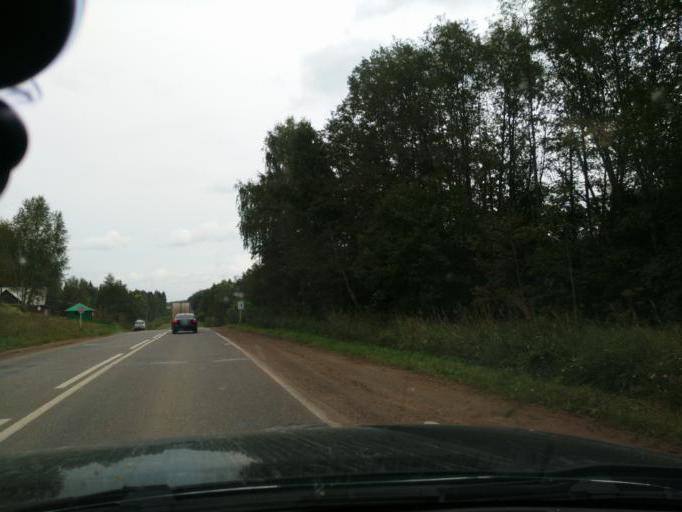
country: RU
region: Perm
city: Kuyeda
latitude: 56.4805
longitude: 55.7817
